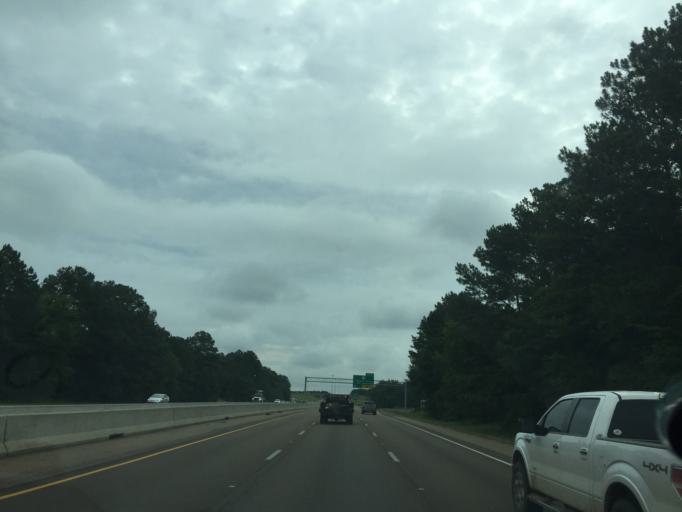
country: US
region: Mississippi
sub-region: Rankin County
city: Pearl
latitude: 32.2697
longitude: -90.0833
